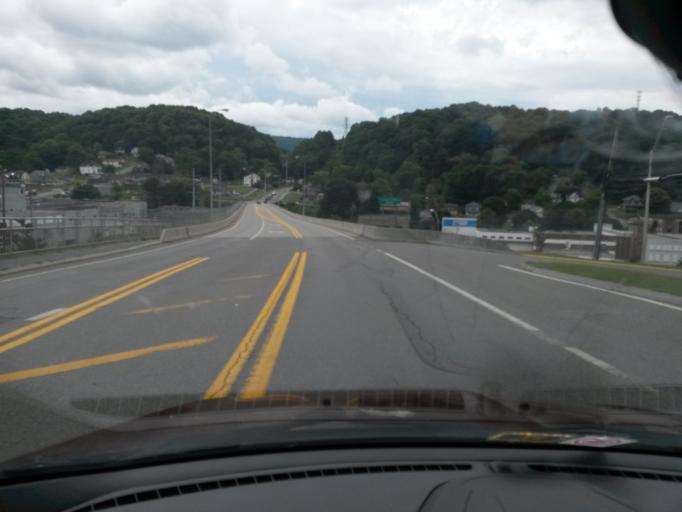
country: US
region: West Virginia
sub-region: Mercer County
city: Bluefield
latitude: 37.2650
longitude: -81.2405
